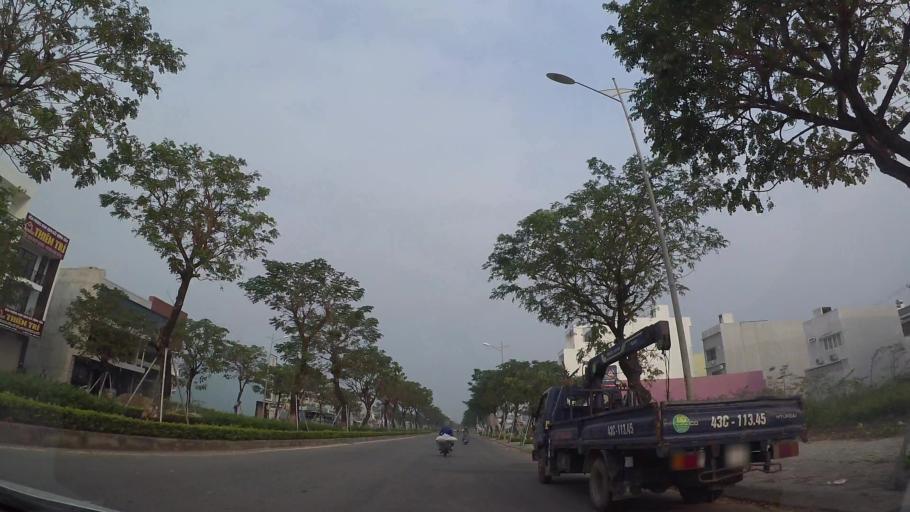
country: VN
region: Da Nang
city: Ngu Hanh Son
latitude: 16.0191
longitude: 108.2296
